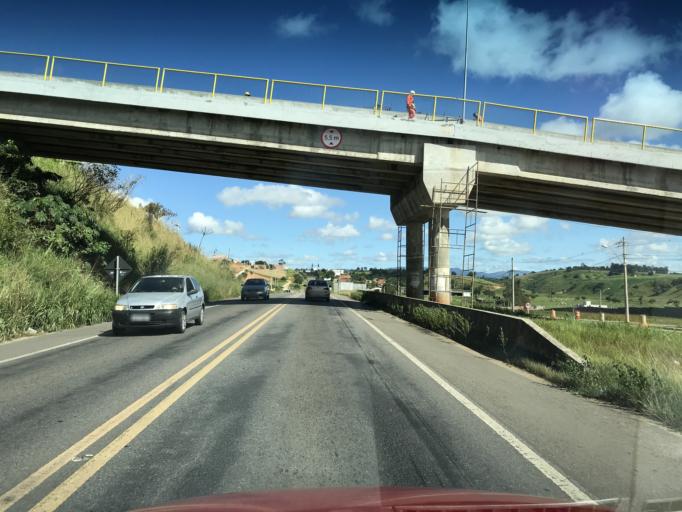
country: BR
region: Bahia
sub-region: Santo Antonio De Jesus
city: Santo Antonio de Jesus
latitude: -12.9556
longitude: -39.2596
